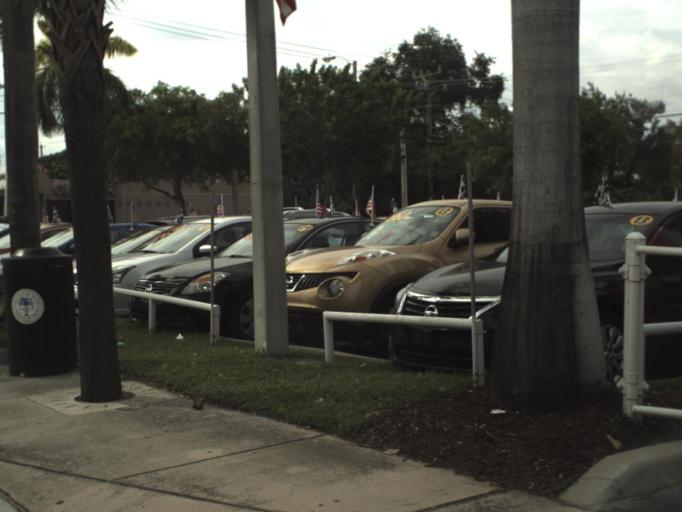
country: US
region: Florida
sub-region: Miami-Dade County
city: West Miami
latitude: 25.7649
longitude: -80.2507
